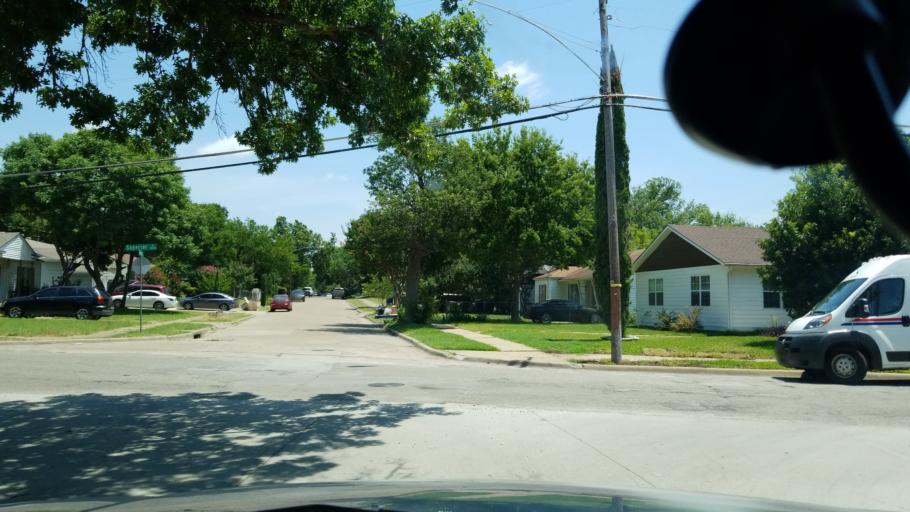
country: US
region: Texas
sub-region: Dallas County
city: Cockrell Hill
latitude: 32.7241
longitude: -96.8640
